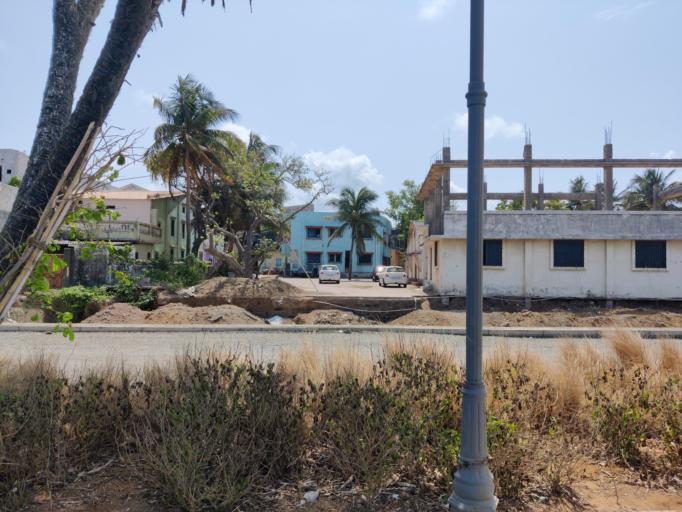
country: IN
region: Daman and Diu
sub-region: Daman District
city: Daman
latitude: 20.4146
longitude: 72.8297
